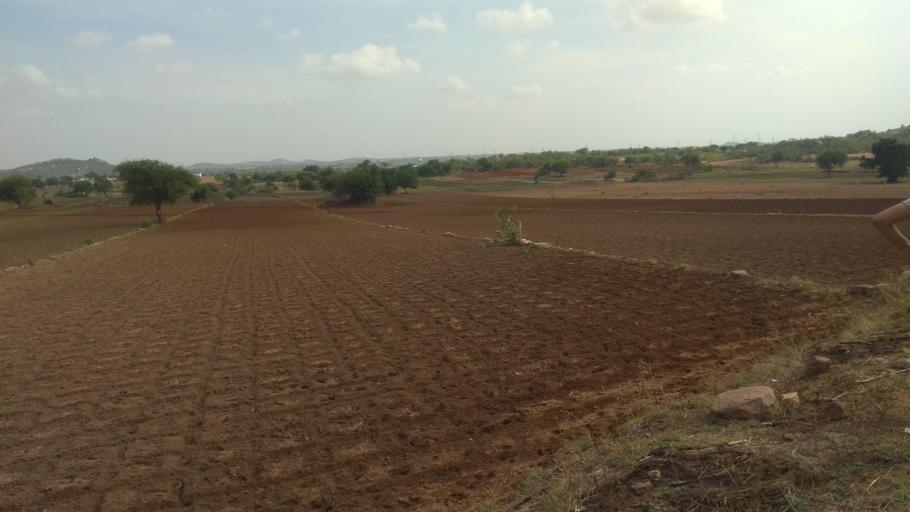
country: IN
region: Telangana
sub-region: Mahbubnagar
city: Farrukhnagar
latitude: 16.8913
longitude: 78.4903
